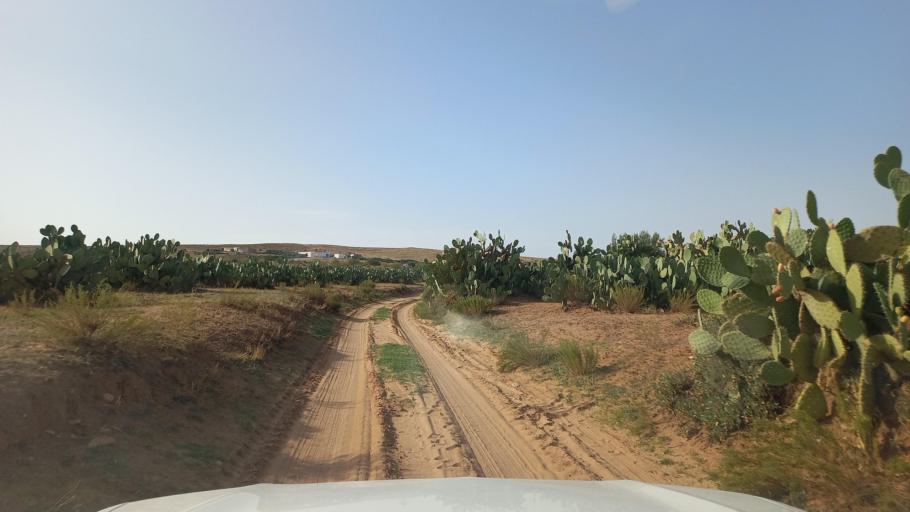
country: TN
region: Al Qasrayn
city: Kasserine
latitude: 35.3602
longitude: 8.8515
